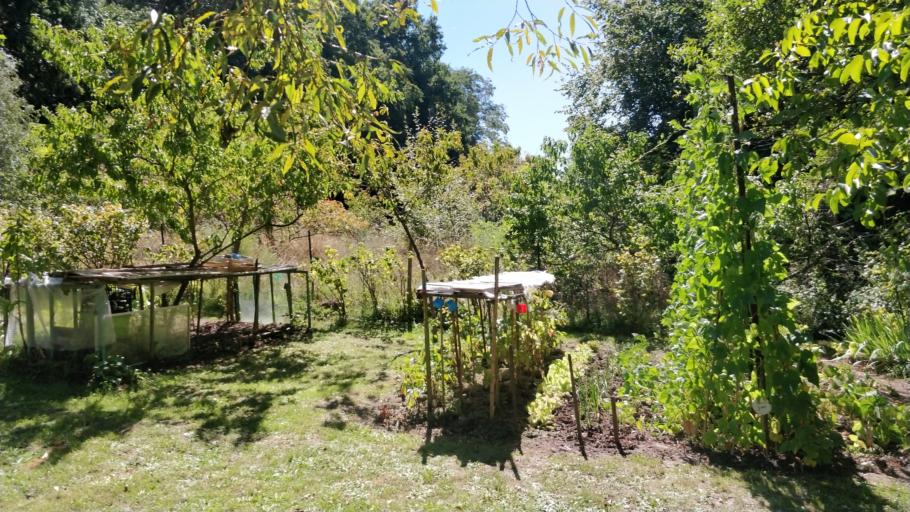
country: FR
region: Ile-de-France
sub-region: Departement de l'Essonne
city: Briis-sous-Forges
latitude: 48.6203
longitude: 2.1204
